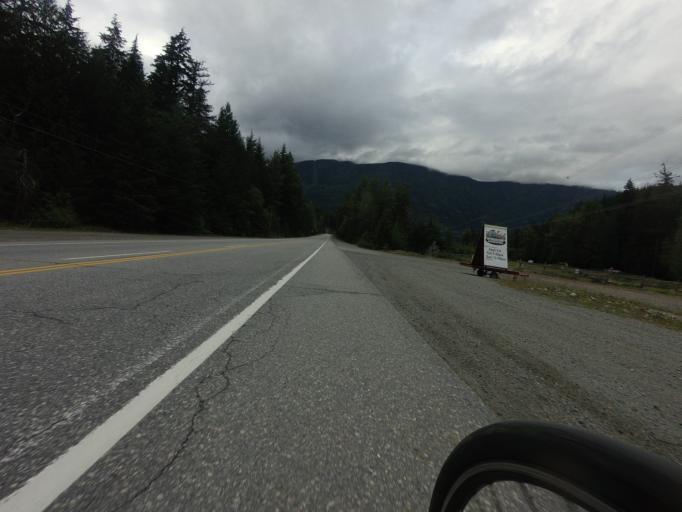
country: CA
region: British Columbia
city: Pemberton
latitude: 50.2555
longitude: -122.8607
